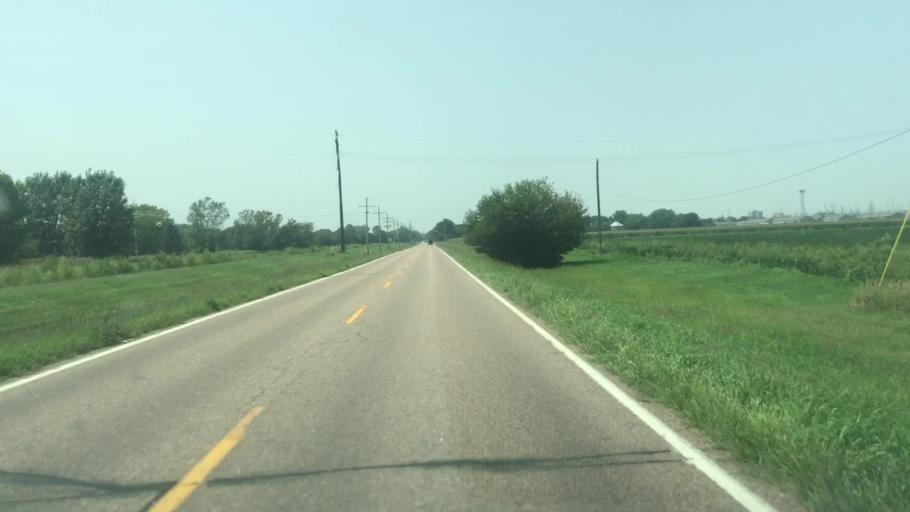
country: US
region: Nebraska
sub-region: Hall County
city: Grand Island
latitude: 40.9164
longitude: -98.3128
